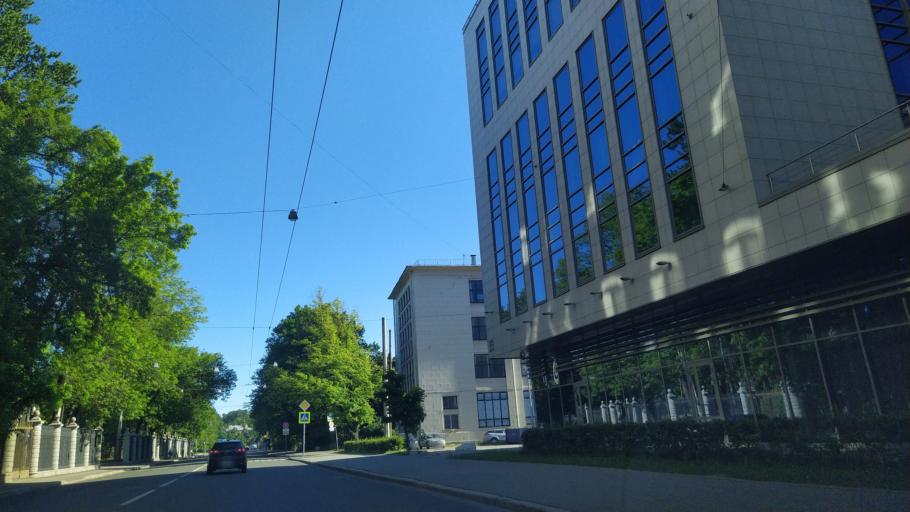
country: RU
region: Leningrad
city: Finlyandskiy
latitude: 59.9638
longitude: 30.3439
